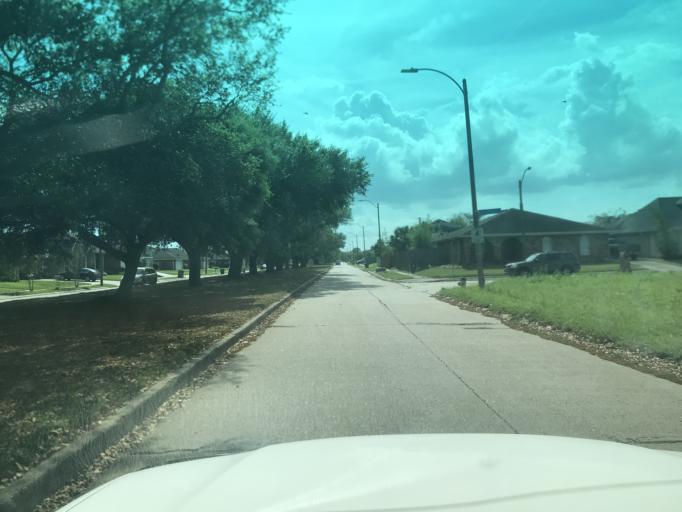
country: US
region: Louisiana
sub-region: Saint Bernard Parish
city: Chalmette
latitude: 30.0382
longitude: -89.9562
